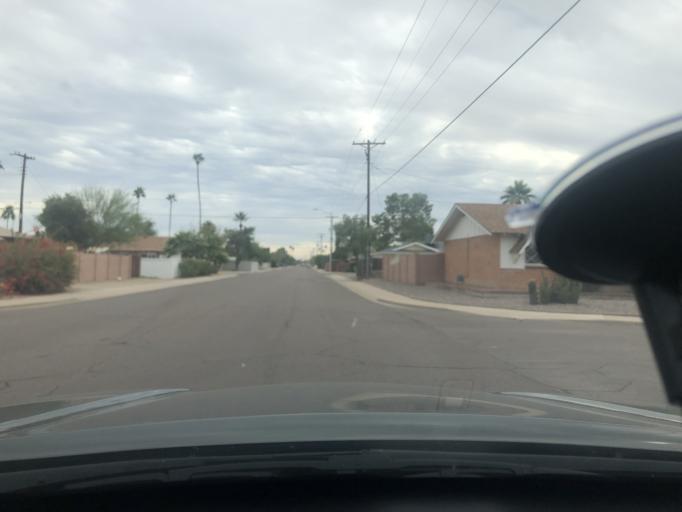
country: US
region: Arizona
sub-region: Maricopa County
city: Scottsdale
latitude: 33.4790
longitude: -111.8961
